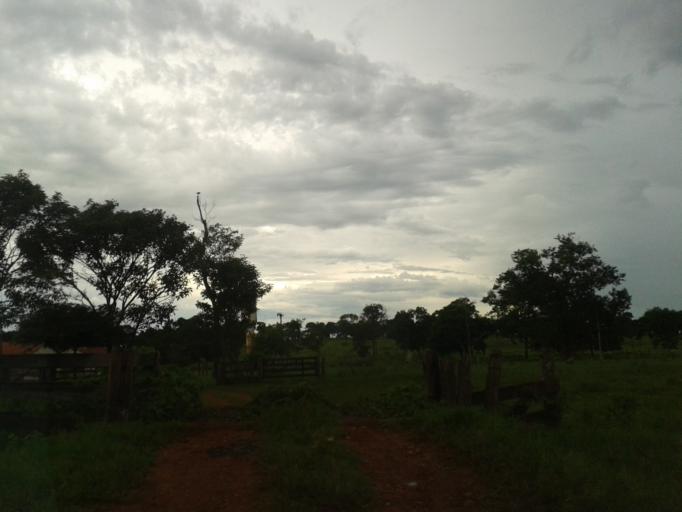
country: BR
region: Minas Gerais
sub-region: Santa Vitoria
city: Santa Vitoria
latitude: -19.2034
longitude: -50.5156
